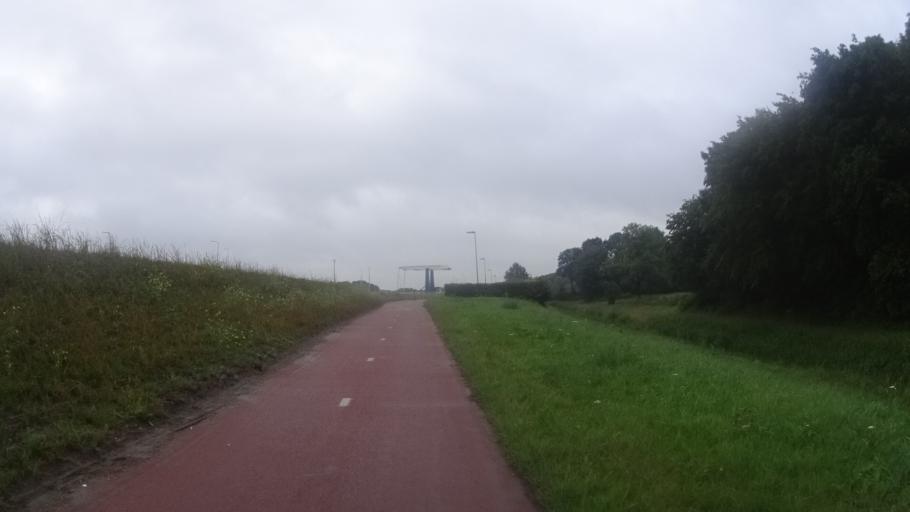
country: NL
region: Groningen
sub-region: Gemeente  Oldambt
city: Winschoten
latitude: 53.1556
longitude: 7.0515
